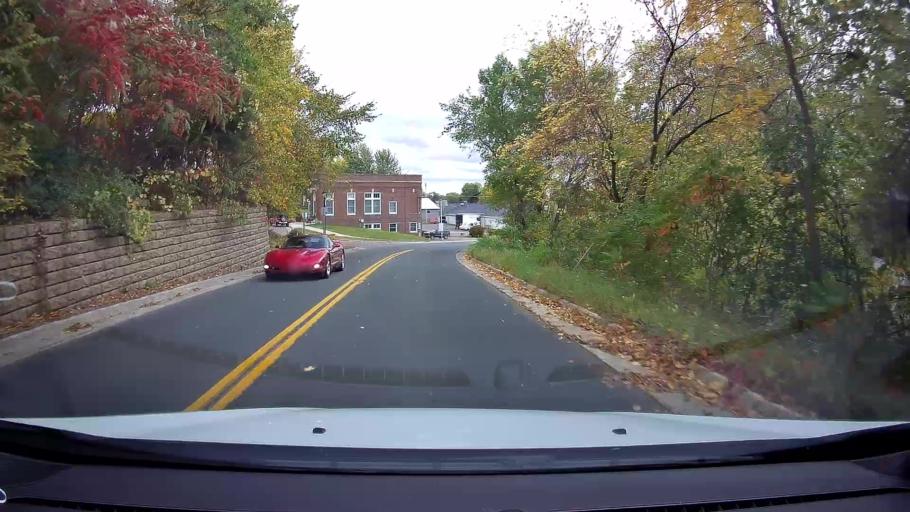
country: US
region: Minnesota
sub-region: Chisago County
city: Center City
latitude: 45.3929
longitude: -92.8172
